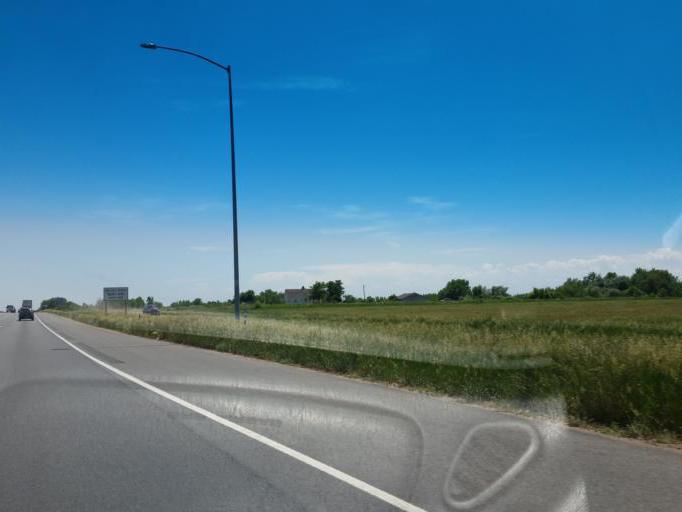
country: US
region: Colorado
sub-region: Larimer County
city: Fort Collins
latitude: 40.5504
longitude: -104.9992
